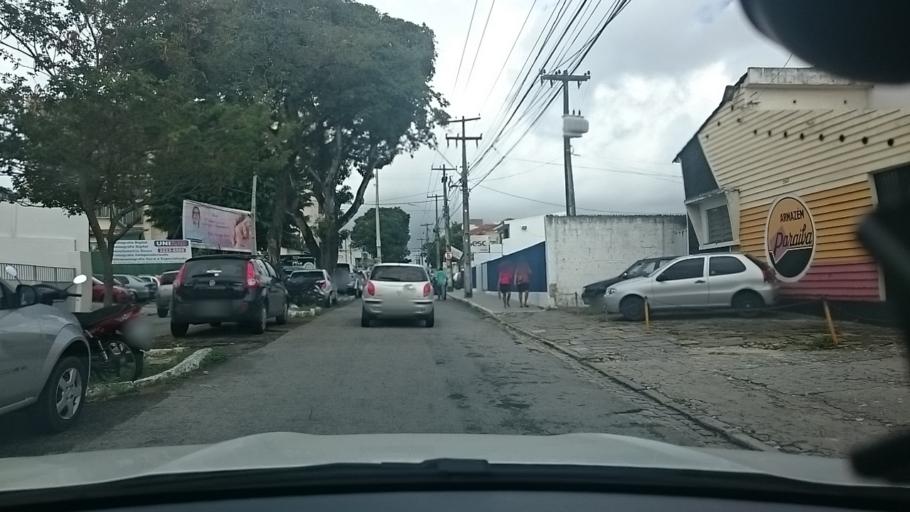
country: BR
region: Paraiba
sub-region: Joao Pessoa
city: Joao Pessoa
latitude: -7.1174
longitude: -34.8775
